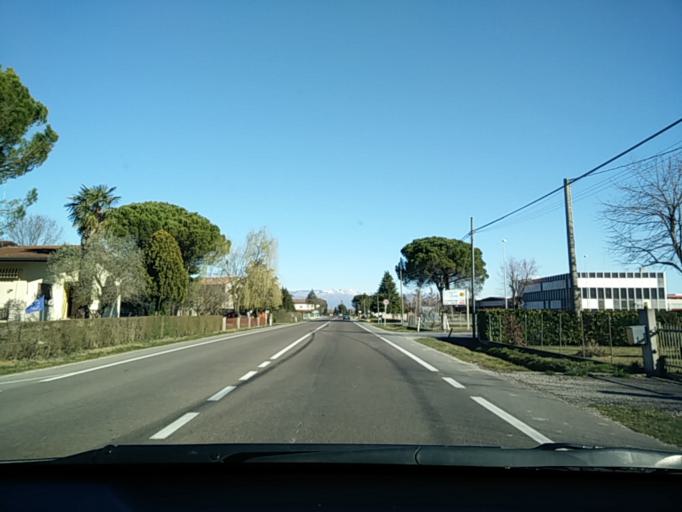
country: IT
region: Veneto
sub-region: Provincia di Treviso
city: Mansue
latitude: 45.8338
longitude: 12.5371
